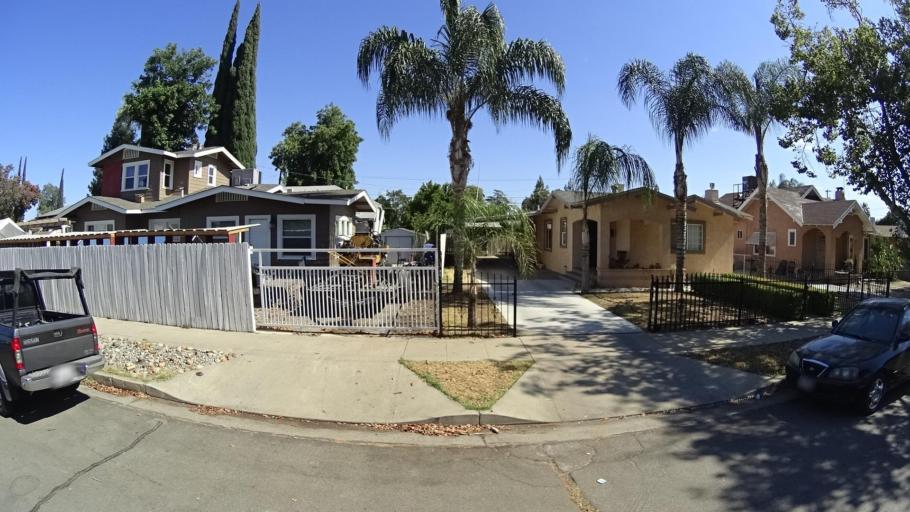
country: US
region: California
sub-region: Fresno County
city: Fresno
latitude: 36.7338
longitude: -119.7671
